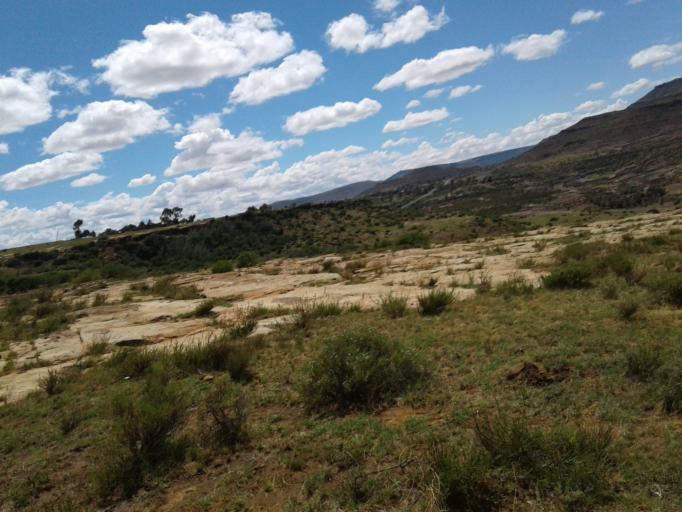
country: LS
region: Quthing
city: Quthing
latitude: -30.3768
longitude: 27.5586
